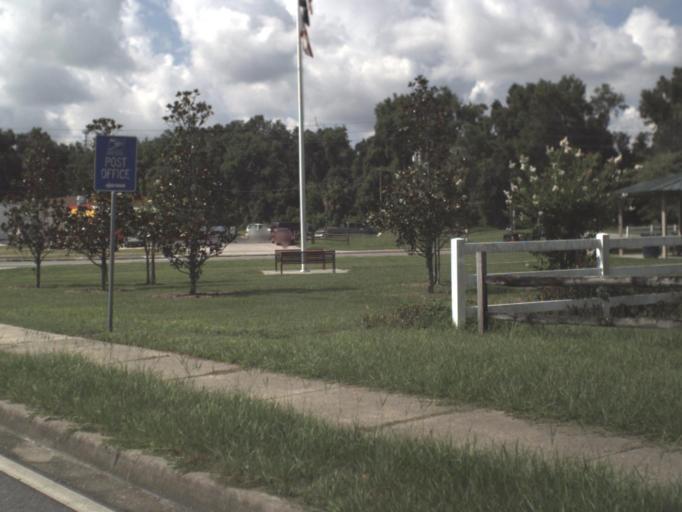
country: US
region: Florida
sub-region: Citrus County
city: Hernando
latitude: 28.8992
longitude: -82.3739
